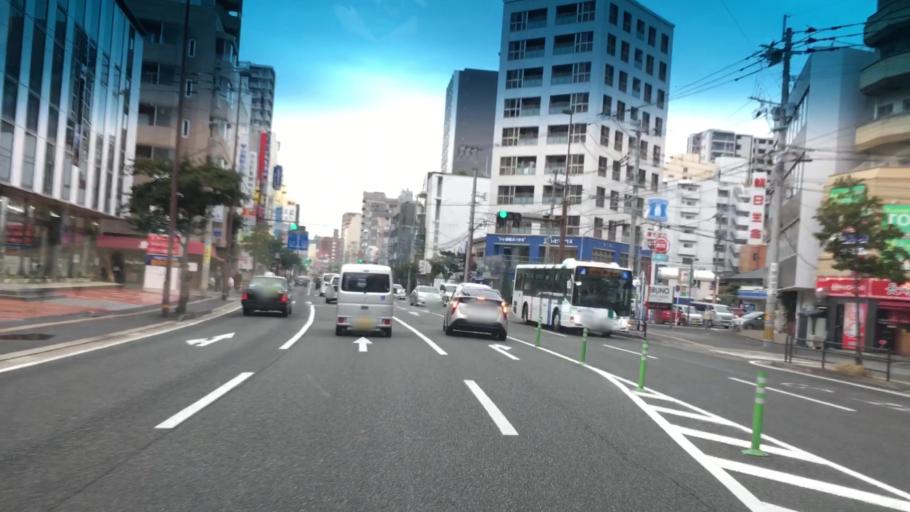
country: JP
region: Fukuoka
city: Fukuoka-shi
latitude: 33.5816
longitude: 130.3996
